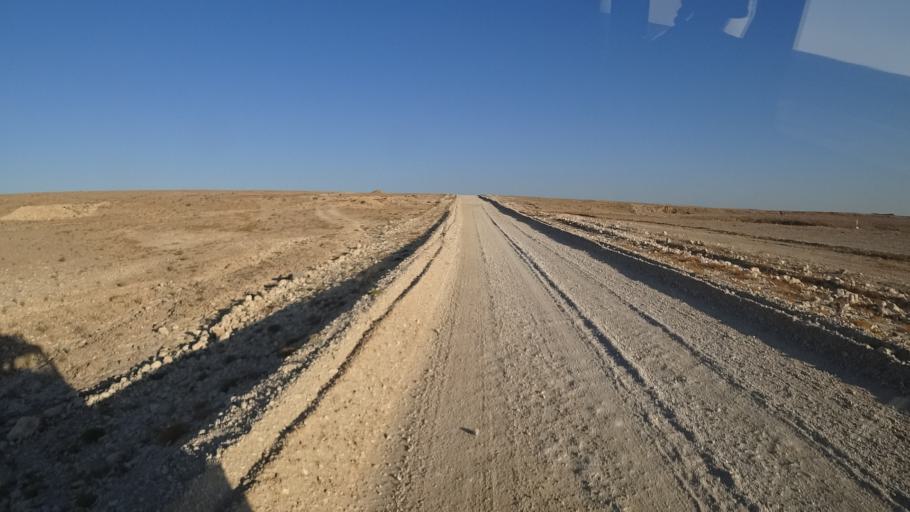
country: YE
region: Al Mahrah
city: Hawf
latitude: 17.1741
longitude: 53.3473
